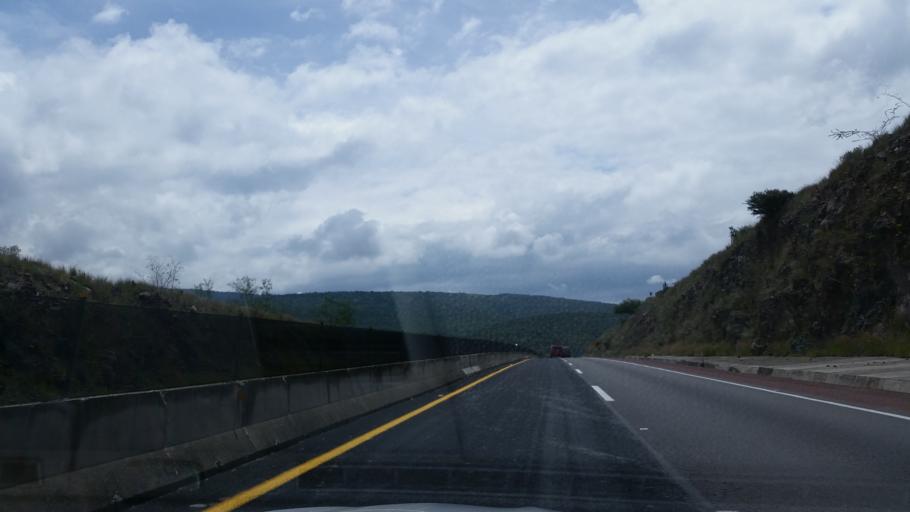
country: MX
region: Hidalgo
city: Tula de Allende
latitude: 20.0556
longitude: -99.3968
